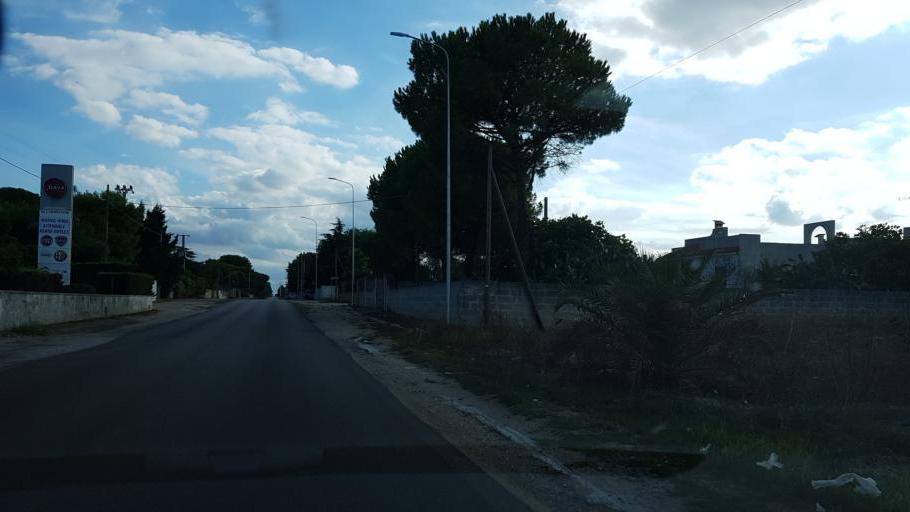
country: IT
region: Apulia
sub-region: Provincia di Lecce
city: Nardo
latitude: 40.1467
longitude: 18.0184
